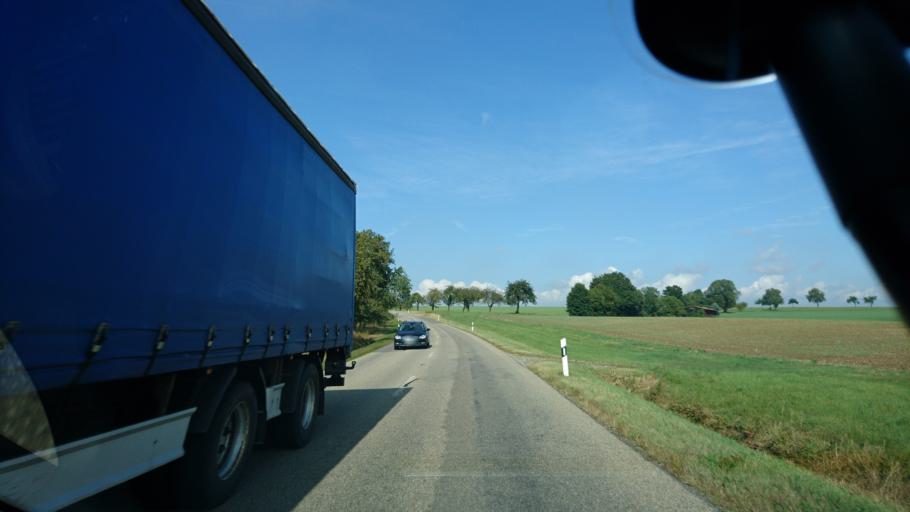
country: DE
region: Baden-Wuerttemberg
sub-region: Regierungsbezirk Stuttgart
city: Wolpertshausen
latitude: 49.1862
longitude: 9.8792
